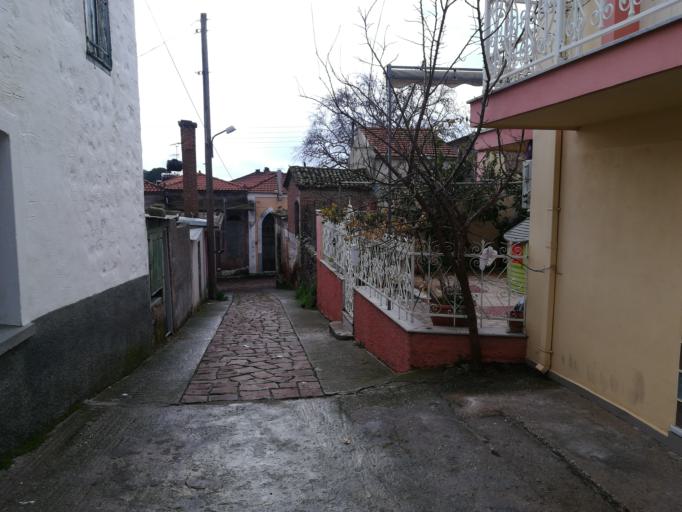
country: GR
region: North Aegean
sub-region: Nomos Lesvou
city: Agia Paraskevi
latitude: 39.2483
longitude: 26.2718
